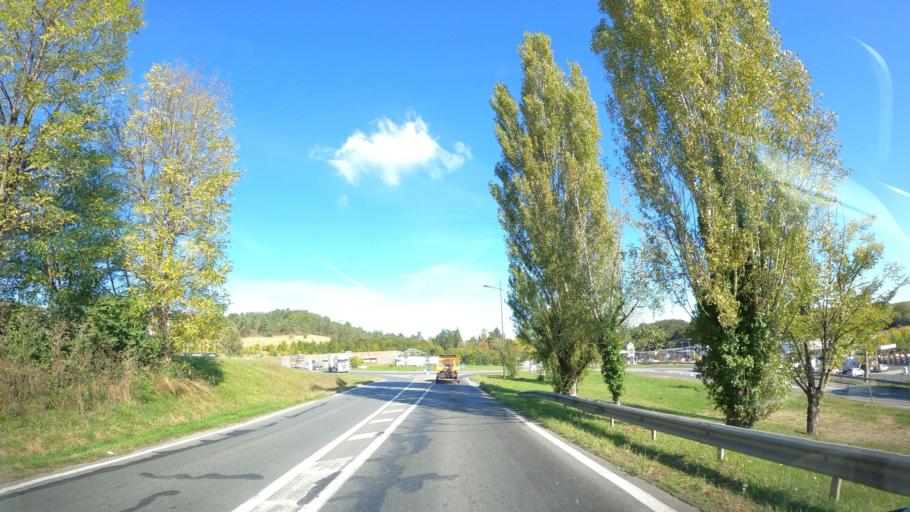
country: FR
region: Aquitaine
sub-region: Departement de la Dordogne
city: Notre-Dame-de-Sanilhac
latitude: 45.1349
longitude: 0.7000
